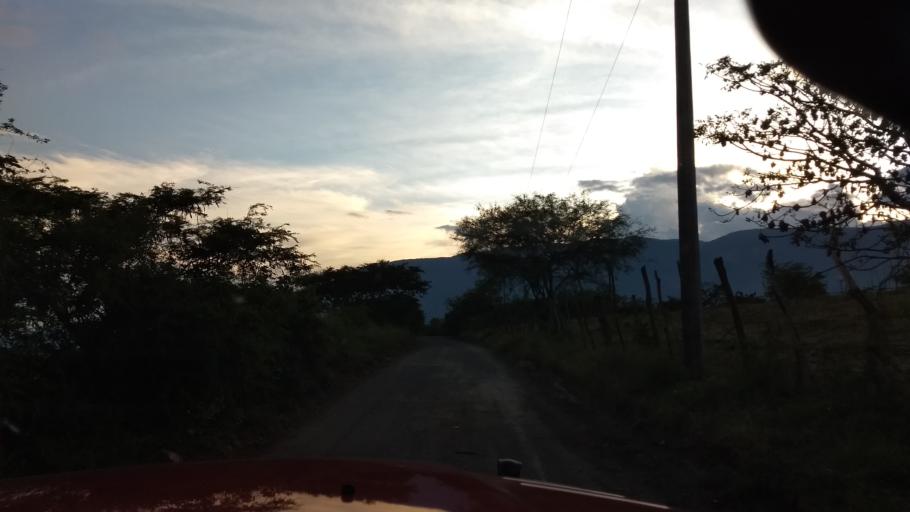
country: MX
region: Colima
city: Suchitlan
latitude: 19.4839
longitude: -103.7963
